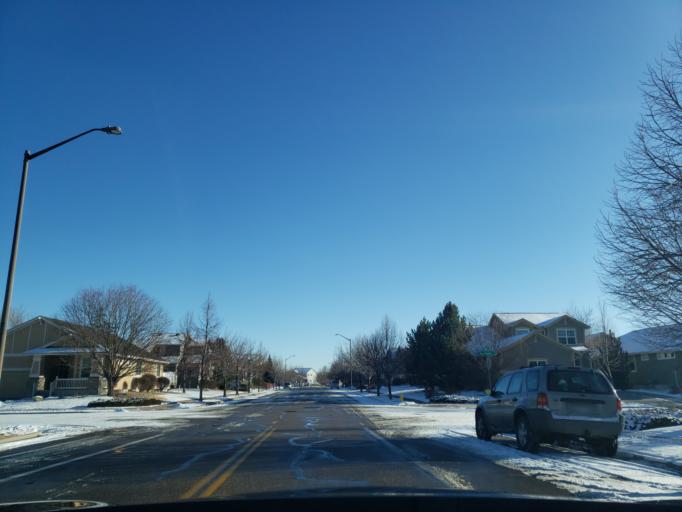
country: US
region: Colorado
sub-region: Larimer County
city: Fort Collins
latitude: 40.5129
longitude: -105.0072
